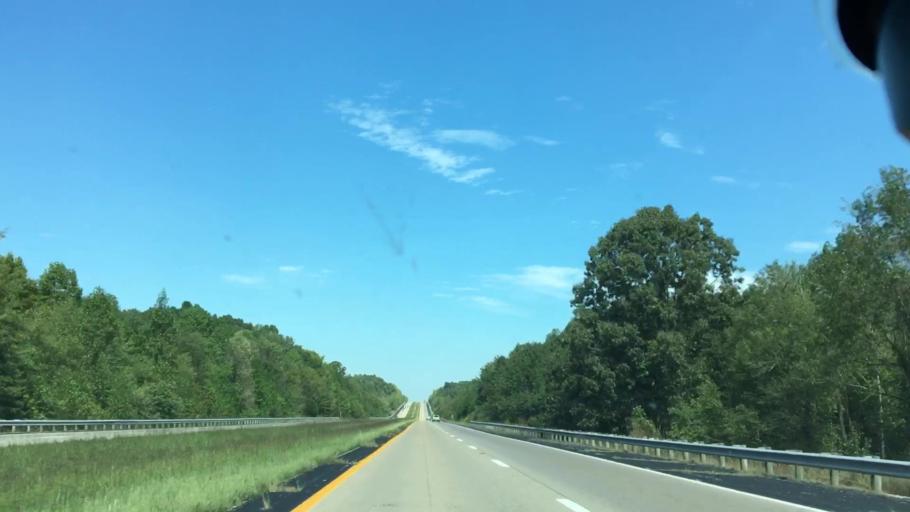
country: US
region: Kentucky
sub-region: Hopkins County
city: Nortonville
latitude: 37.0962
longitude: -87.4615
